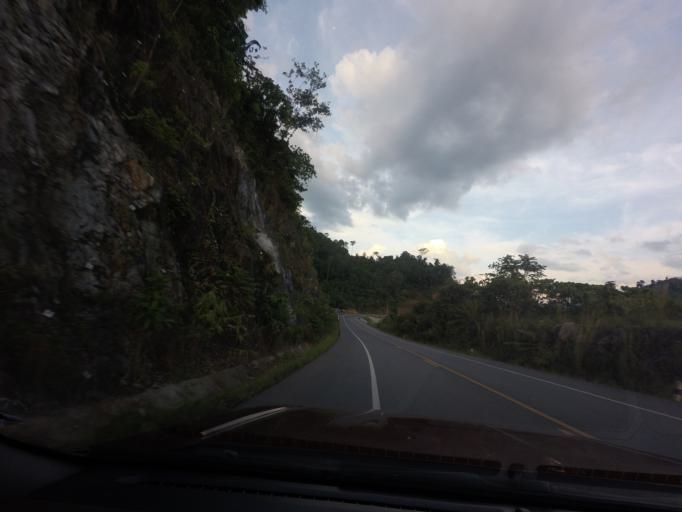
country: TH
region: Yala
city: Than To
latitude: 6.0520
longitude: 101.1957
